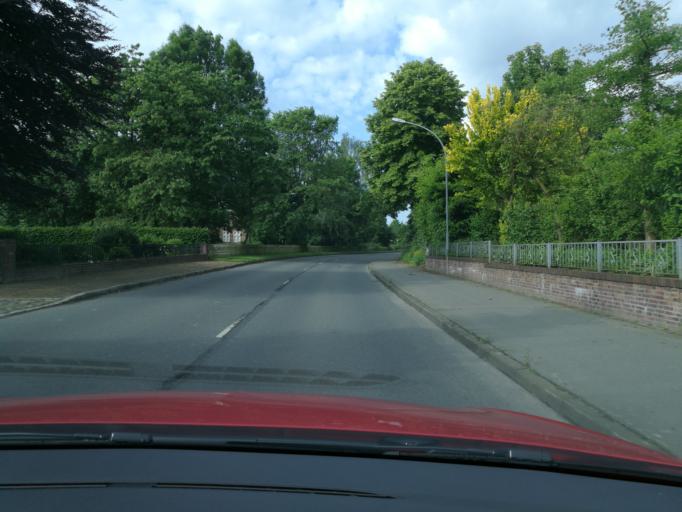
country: DE
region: Schleswig-Holstein
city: Hoisdorf
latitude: 53.6745
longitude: 10.3316
